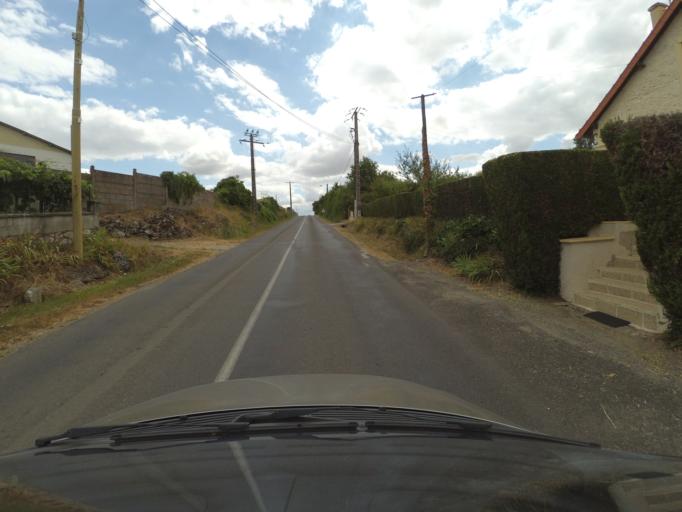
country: FR
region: Poitou-Charentes
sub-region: Departement de la Vienne
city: Saint-Savin
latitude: 46.5656
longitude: 0.8795
